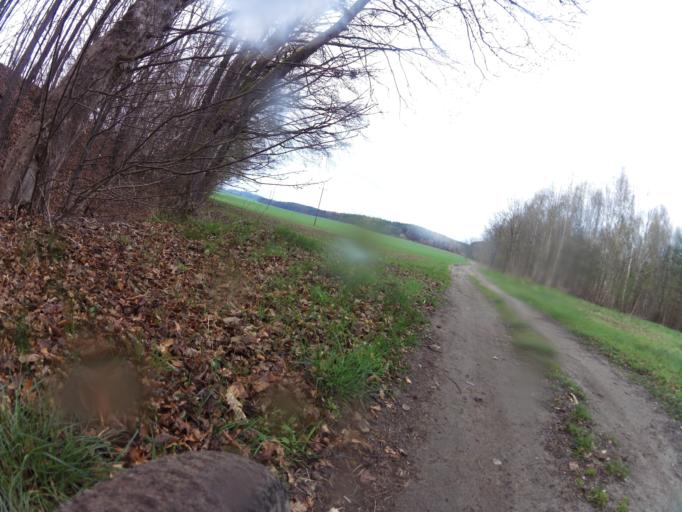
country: PL
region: West Pomeranian Voivodeship
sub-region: Powiat koszalinski
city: Polanow
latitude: 54.2145
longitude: 16.7298
